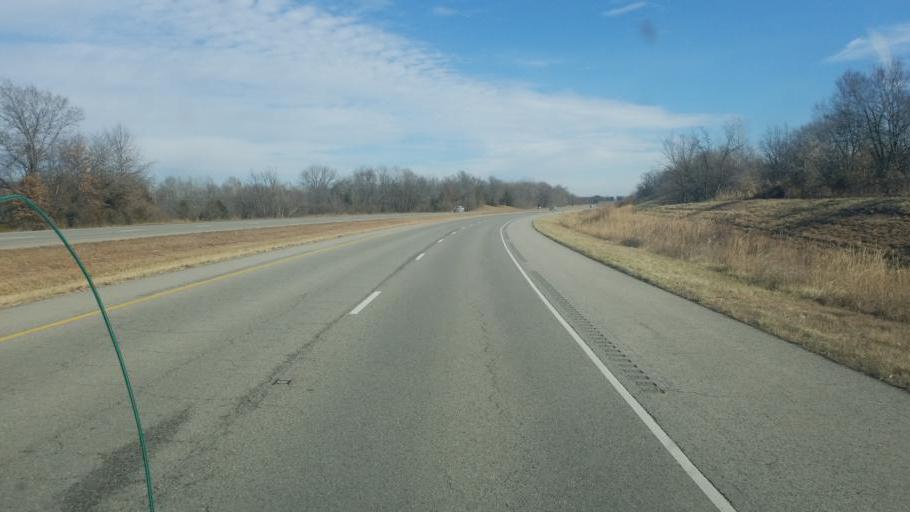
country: US
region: Illinois
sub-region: Williamson County
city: Marion
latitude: 37.7325
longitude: -88.8150
